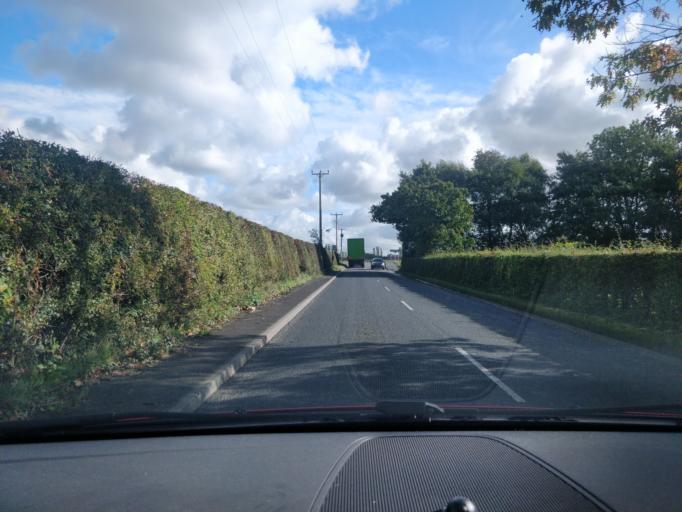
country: GB
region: England
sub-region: Lancashire
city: Ormskirk
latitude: 53.5909
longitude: -2.8862
